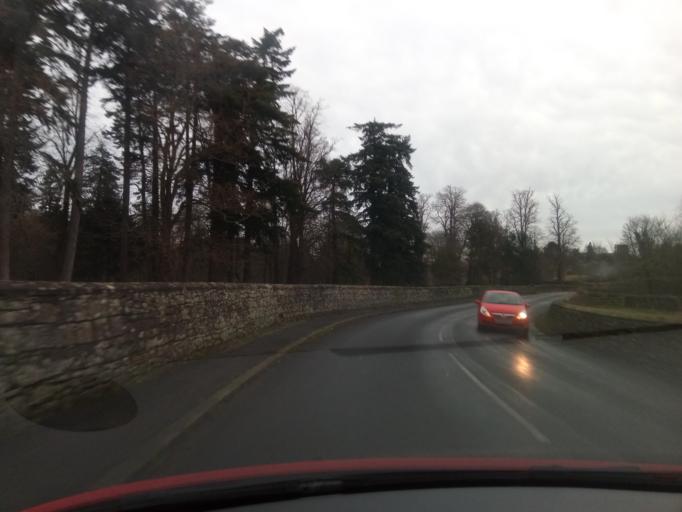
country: GB
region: England
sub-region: Northumberland
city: Alnwick
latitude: 55.4204
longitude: -1.7170
